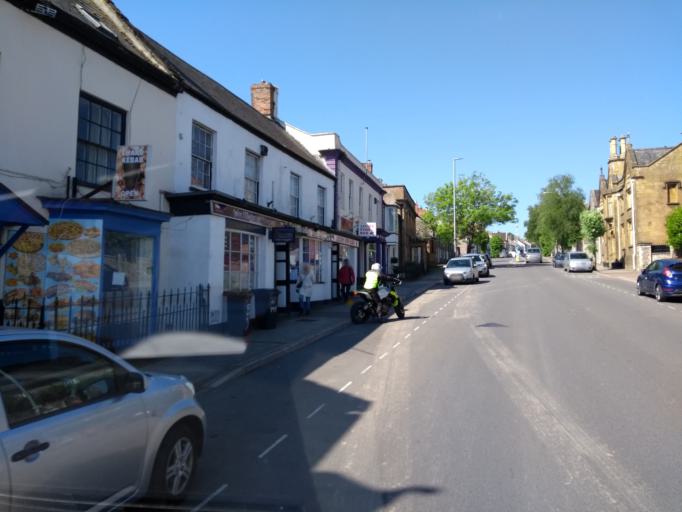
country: GB
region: England
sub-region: Somerset
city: Chard
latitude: 50.8726
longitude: -2.9666
